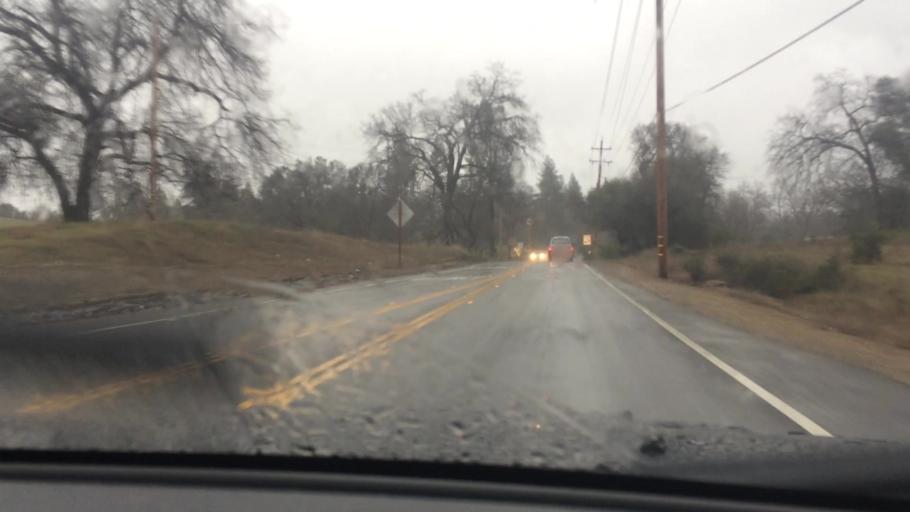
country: US
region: California
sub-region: El Dorado County
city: Deer Park
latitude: 38.6902
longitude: -120.8301
